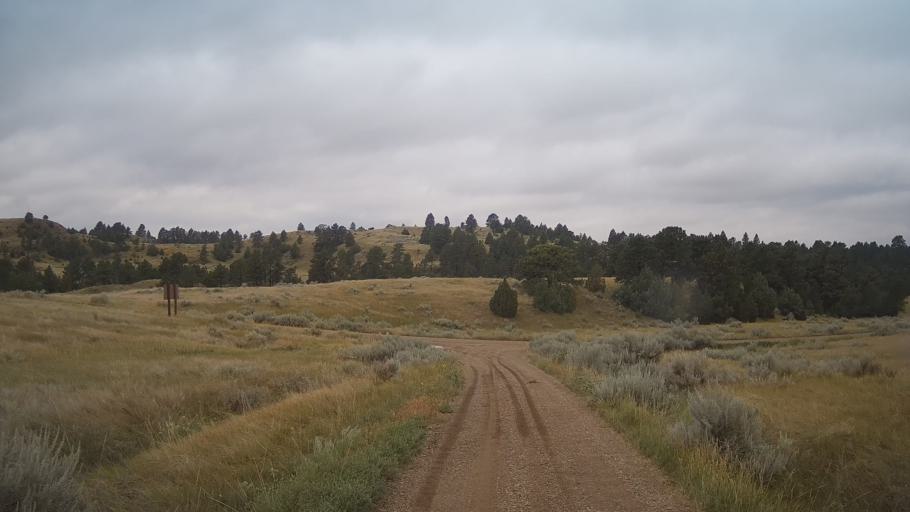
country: US
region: Montana
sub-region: Dawson County
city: Glendive
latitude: 47.0578
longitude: -104.6705
